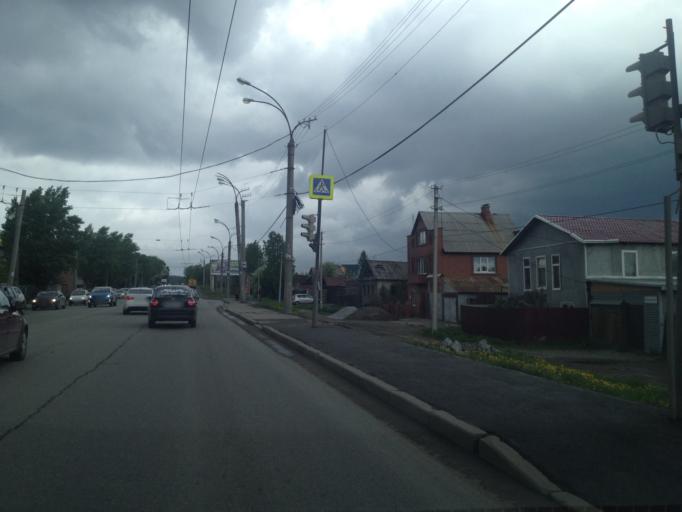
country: RU
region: Sverdlovsk
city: Istok
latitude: 56.7491
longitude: 60.6810
